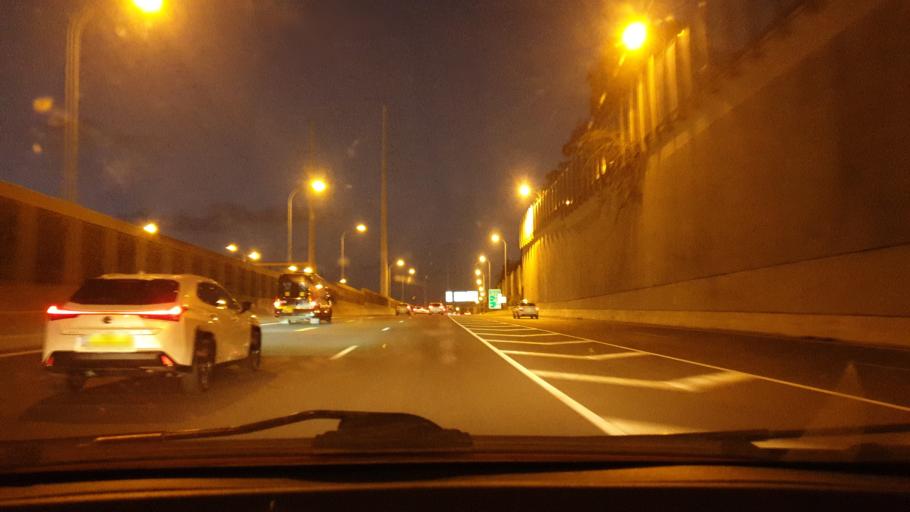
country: IL
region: Tel Aviv
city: Bat Yam
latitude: 32.0251
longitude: 34.7608
